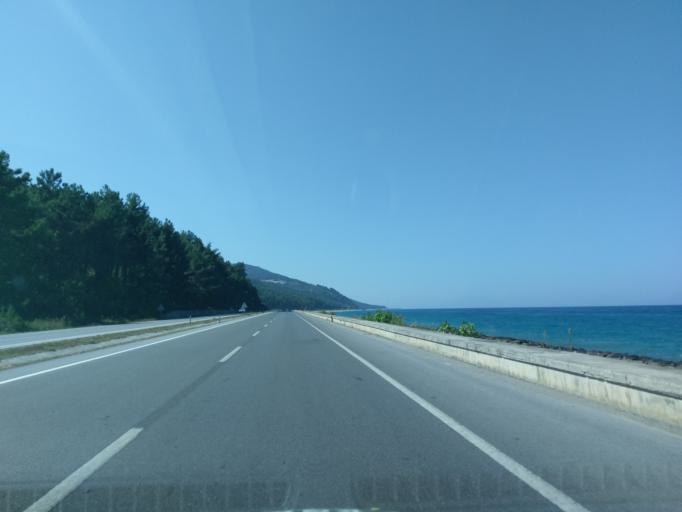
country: TR
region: Samsun
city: Yakakent
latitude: 41.6478
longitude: 35.4673
